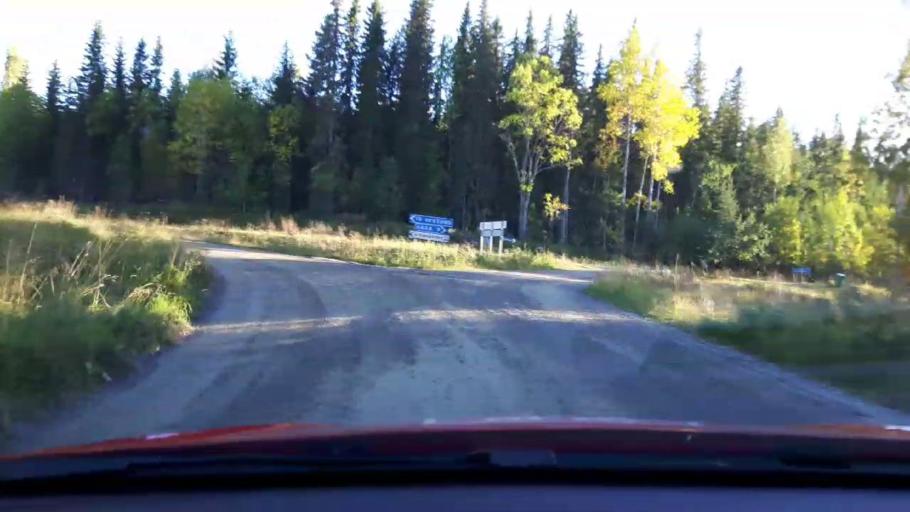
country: SE
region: Jaemtland
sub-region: OEstersunds Kommun
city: Brunflo
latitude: 62.9457
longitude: 14.9832
